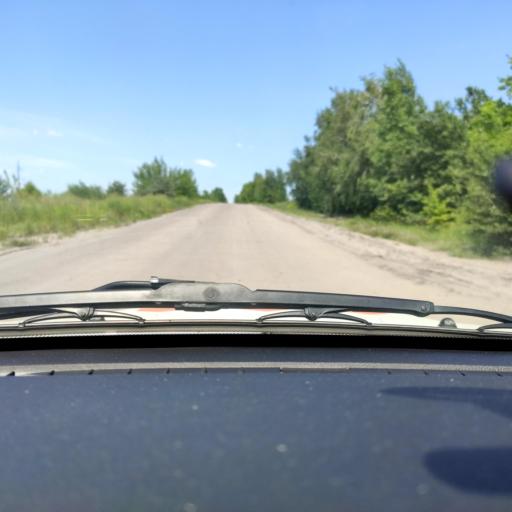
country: RU
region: Voronezj
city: Devitsa
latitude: 51.6269
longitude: 38.9531
